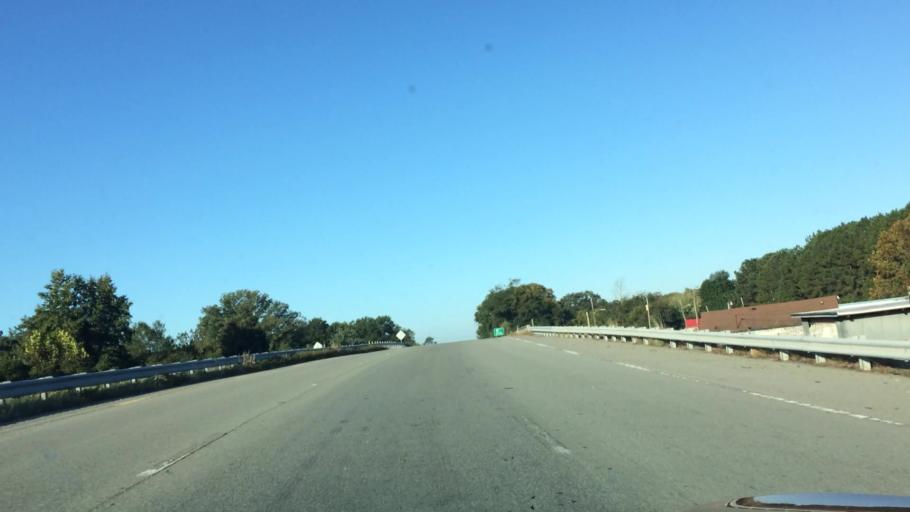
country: US
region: North Carolina
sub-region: Wayne County
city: Goldsboro
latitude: 35.3993
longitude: -77.9933
